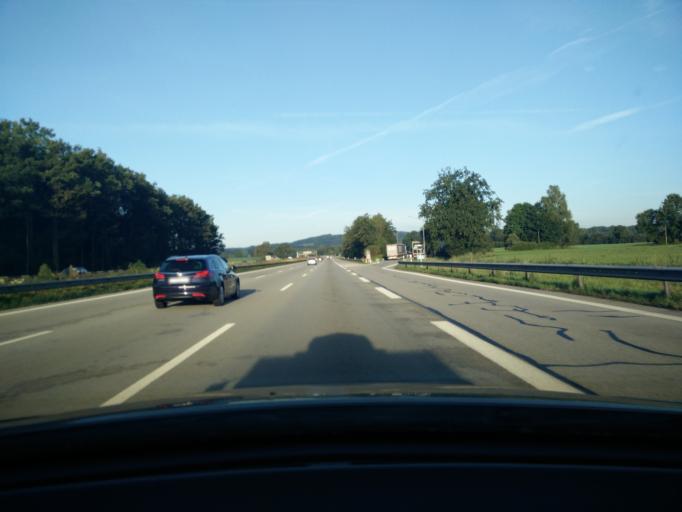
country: DE
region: Bavaria
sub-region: Upper Bavaria
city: Bad Aibling
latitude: 47.8214
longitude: 12.0014
